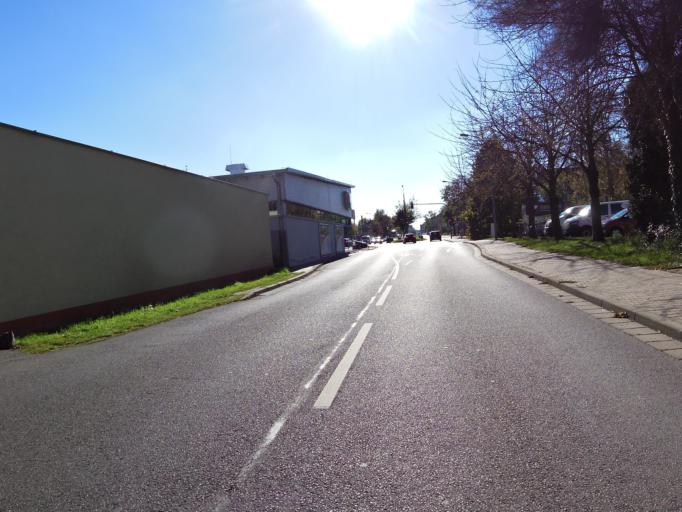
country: DE
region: Saxony
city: Leipzig
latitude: 51.3767
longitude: 12.3784
